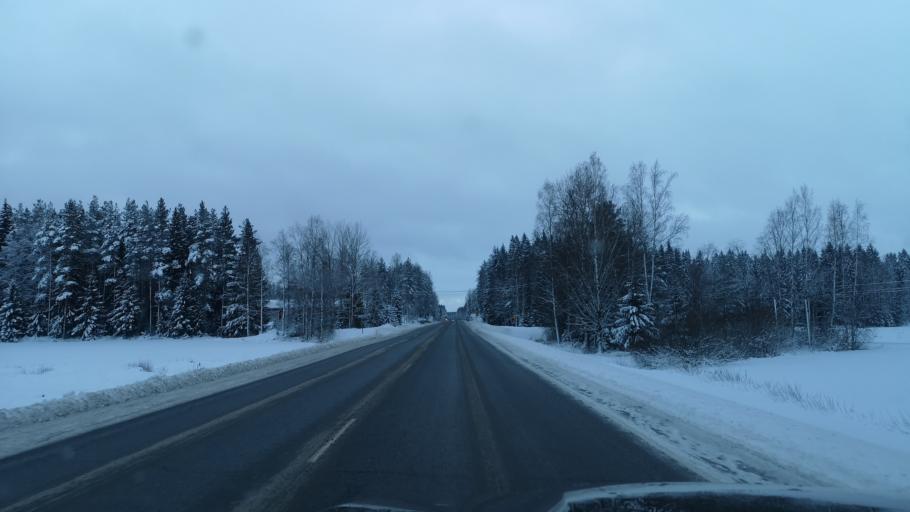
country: FI
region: Varsinais-Suomi
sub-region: Loimaa
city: Loimaa
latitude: 60.9156
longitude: 23.1876
